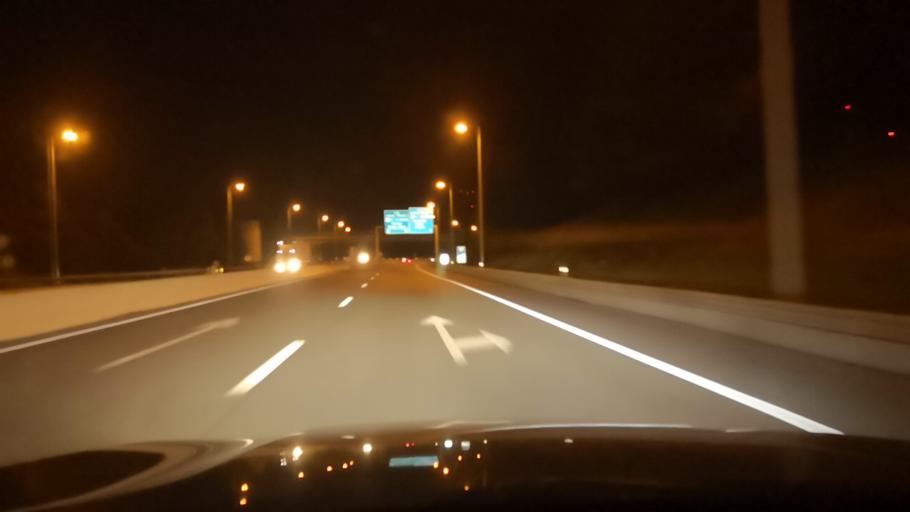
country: PT
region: Setubal
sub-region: Palmela
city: Palmela
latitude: 38.5722
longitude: -8.8664
